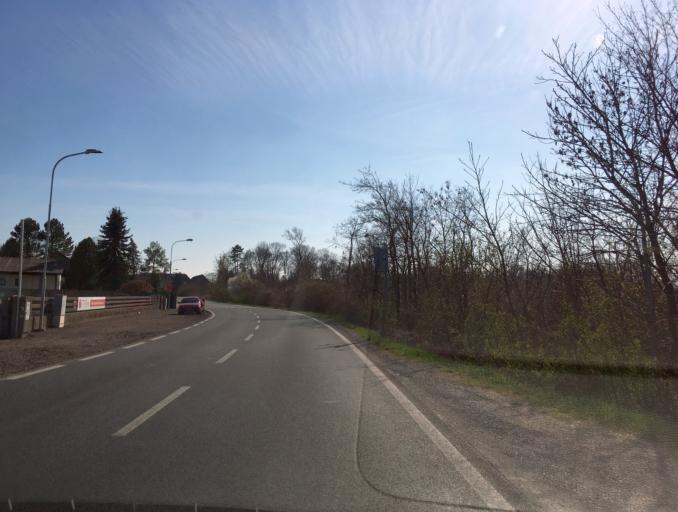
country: AT
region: Lower Austria
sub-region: Politischer Bezirk Wien-Umgebung
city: Schwadorf
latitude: 48.0545
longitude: 16.6082
